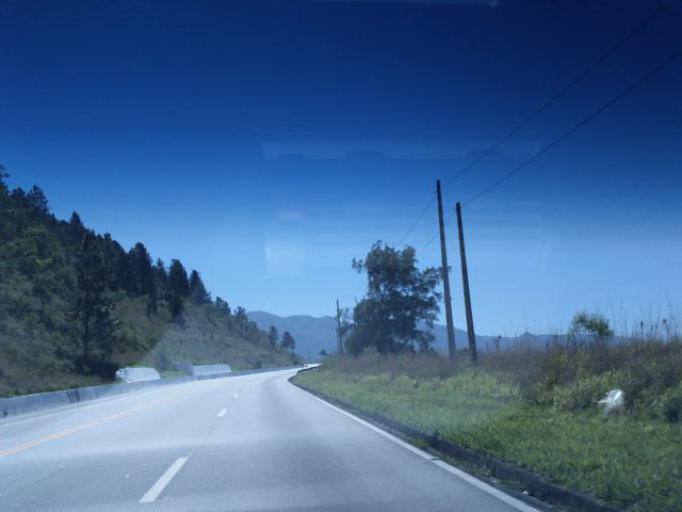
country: BR
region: Sao Paulo
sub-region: Campos Do Jordao
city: Campos do Jordao
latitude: -22.8516
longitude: -45.6150
